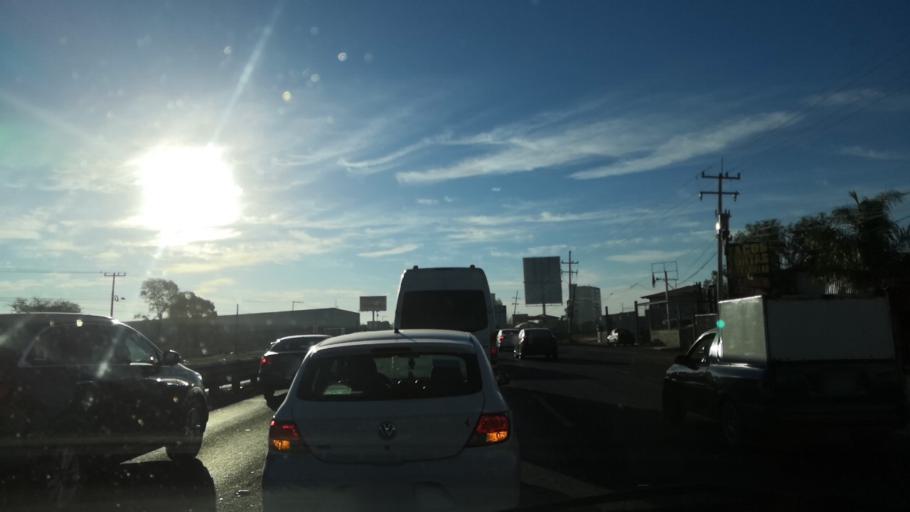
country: MX
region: Guanajuato
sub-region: Silao de la Victoria
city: San Antonio Texas
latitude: 20.9906
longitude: -101.4943
